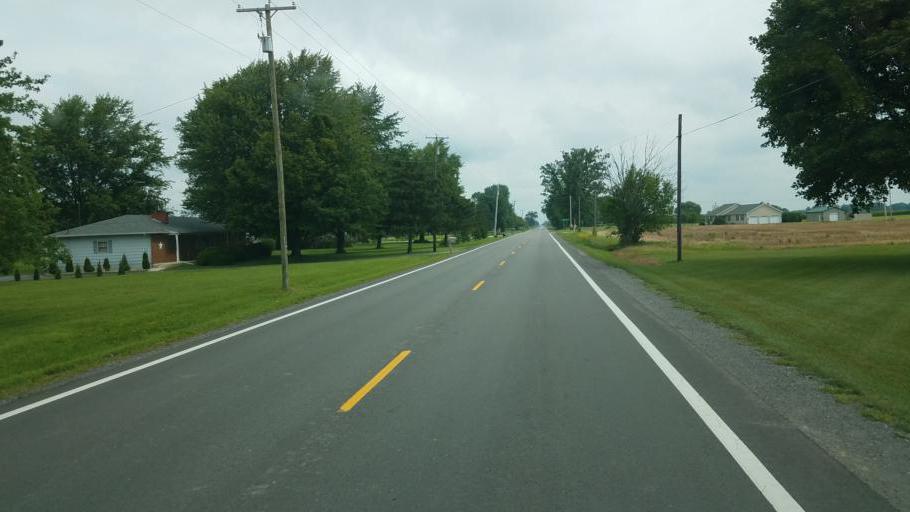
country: US
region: Ohio
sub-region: Marion County
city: Marion
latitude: 40.6360
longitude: -83.0239
